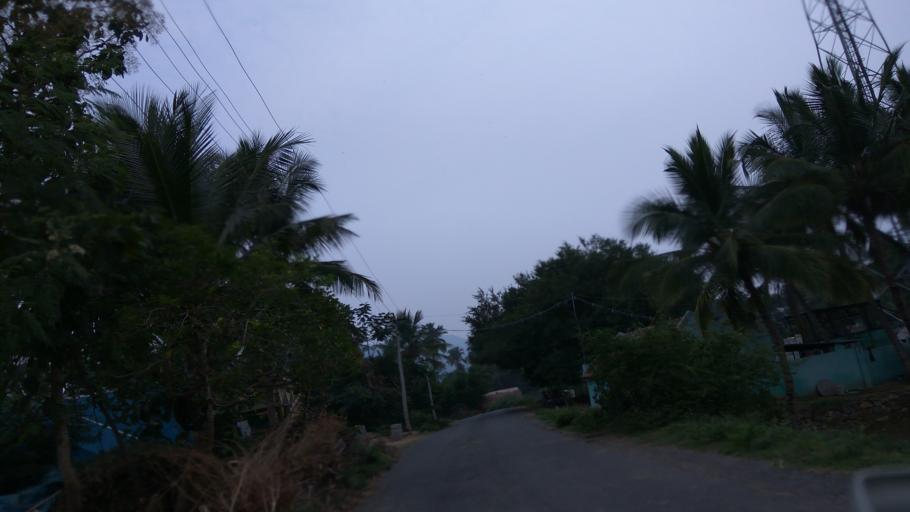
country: IN
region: Tamil Nadu
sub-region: Dharmapuri
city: Dharmapuri
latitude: 12.0216
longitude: 78.1162
